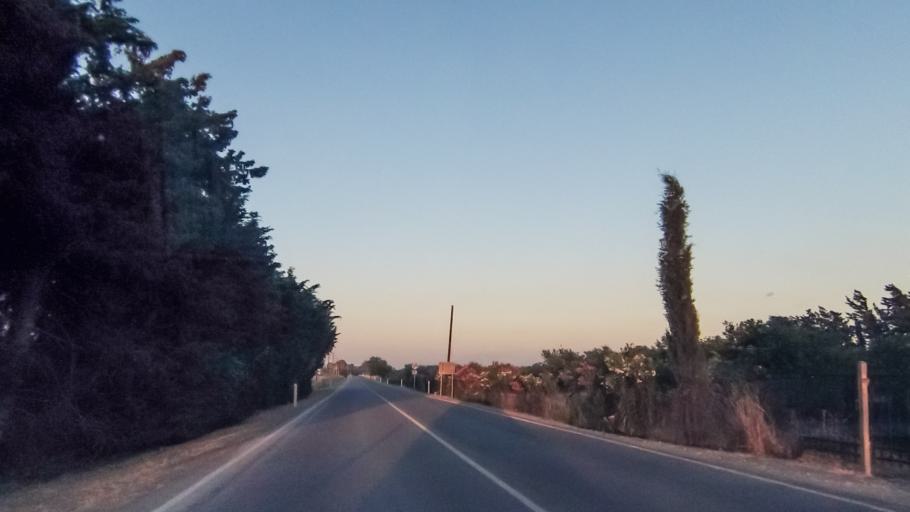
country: CY
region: Larnaka
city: Kolossi
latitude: 34.6574
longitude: 32.9170
